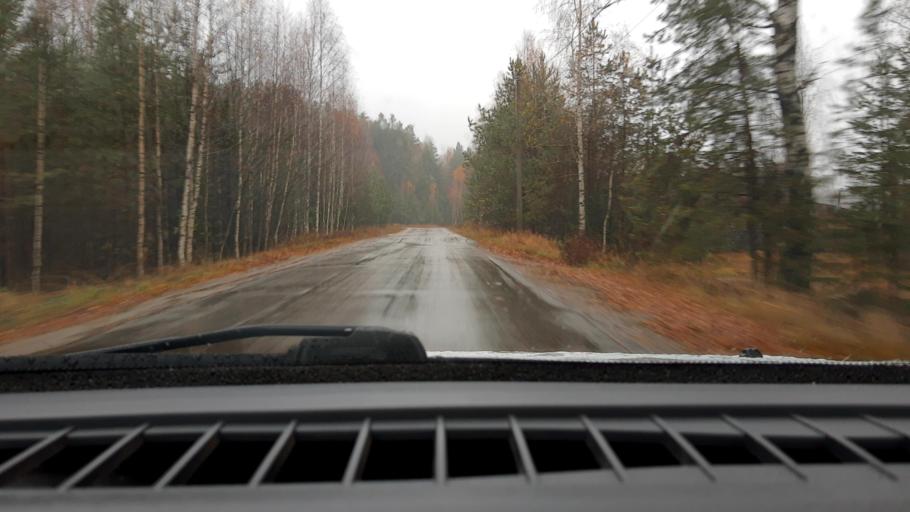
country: RU
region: Nizjnij Novgorod
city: Linda
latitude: 56.6912
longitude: 44.2031
